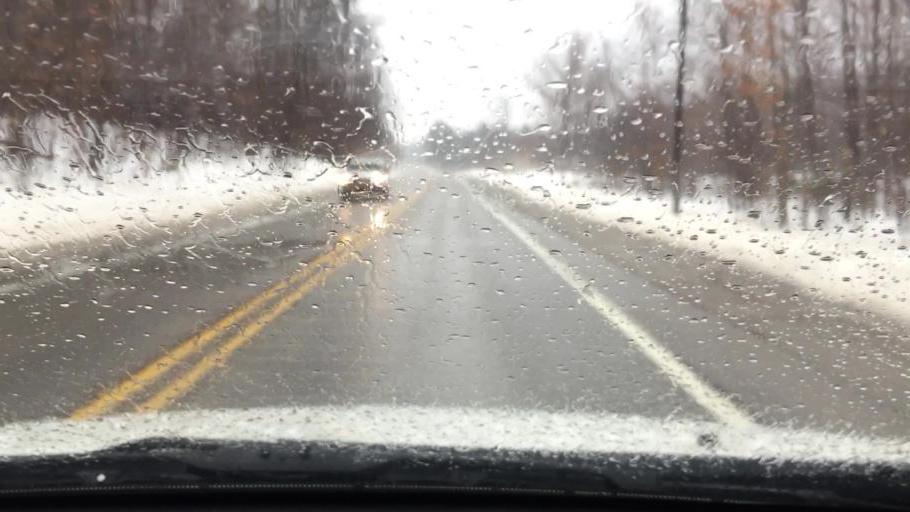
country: US
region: Michigan
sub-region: Charlevoix County
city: East Jordan
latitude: 45.2211
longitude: -85.1755
